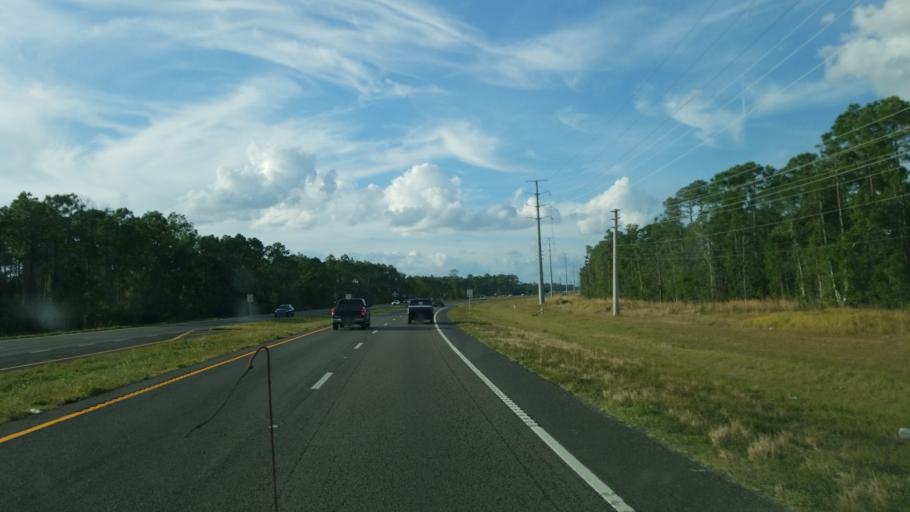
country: US
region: Florida
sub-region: Osceola County
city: Saint Cloud
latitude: 28.1973
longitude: -81.1644
